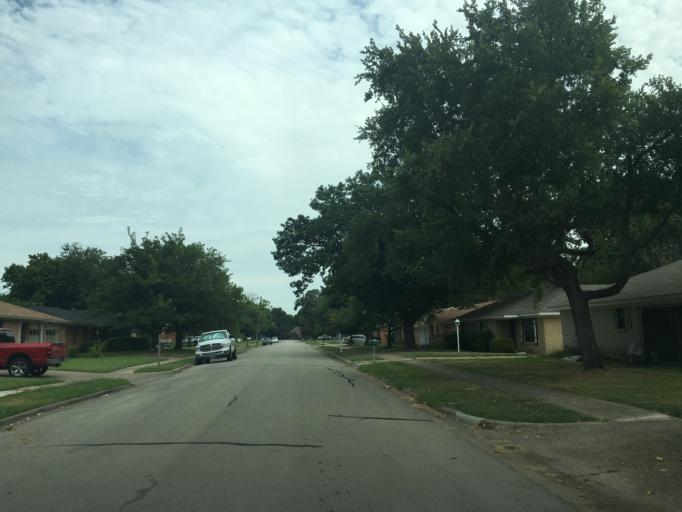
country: US
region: Texas
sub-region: Collin County
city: Wylie
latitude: 33.0091
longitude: -96.5339
